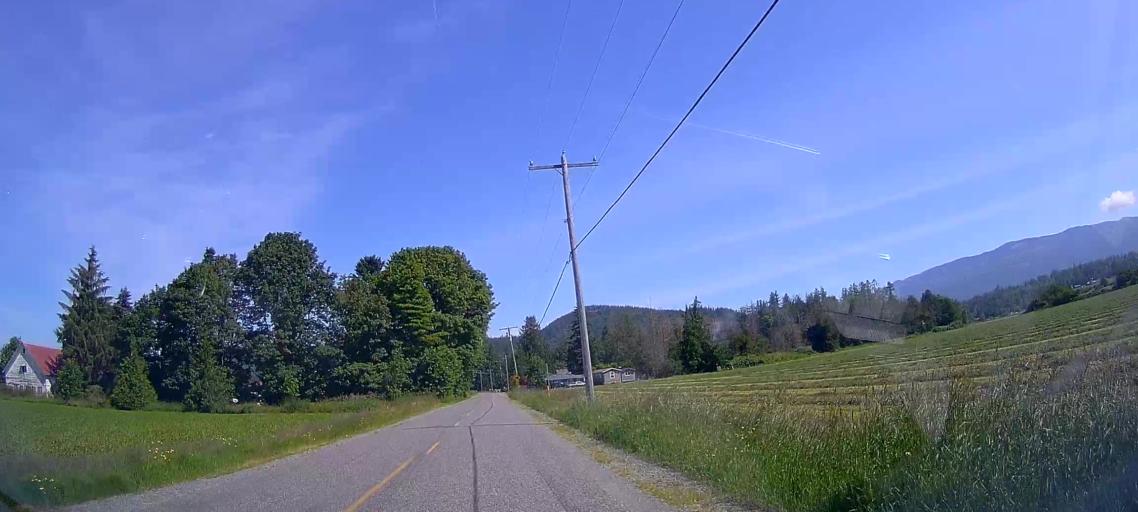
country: US
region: Washington
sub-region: Skagit County
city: Burlington
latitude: 48.5199
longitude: -122.2908
